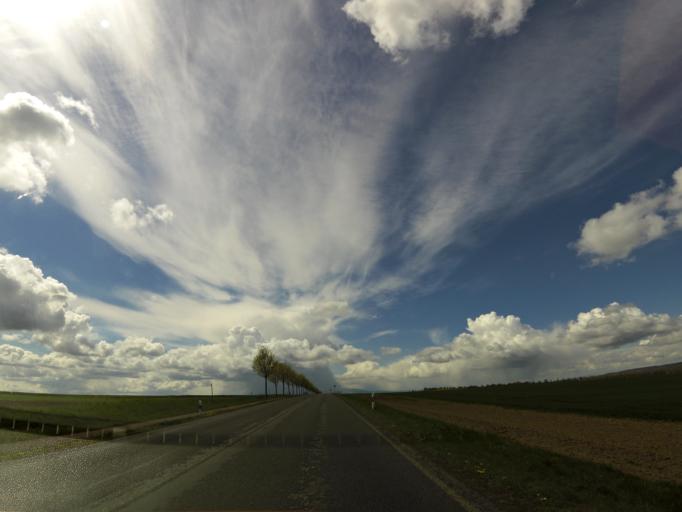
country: DE
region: Saxony-Anhalt
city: Gross Quenstedt
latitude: 51.9109
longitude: 11.1114
